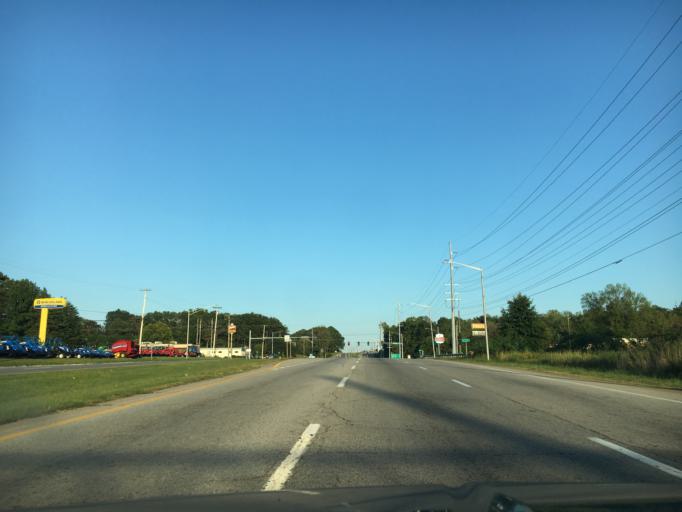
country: US
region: Virginia
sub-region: City of Danville
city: Danville
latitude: 36.5831
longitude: -79.3552
